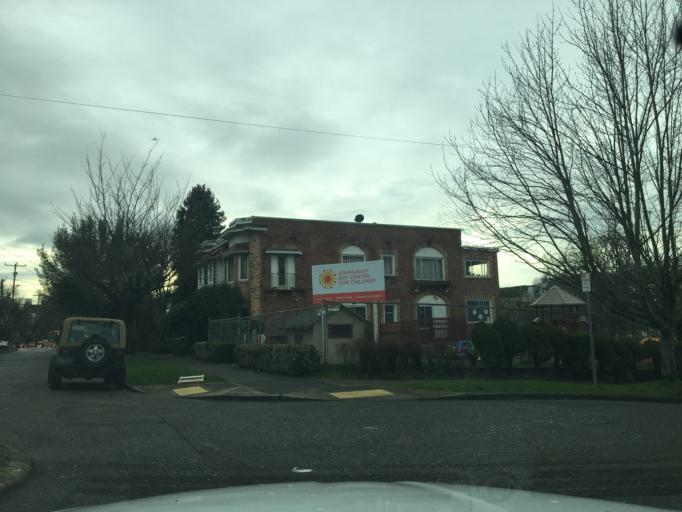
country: US
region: Washington
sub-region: King County
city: Seattle
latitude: 47.6037
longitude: -122.3038
